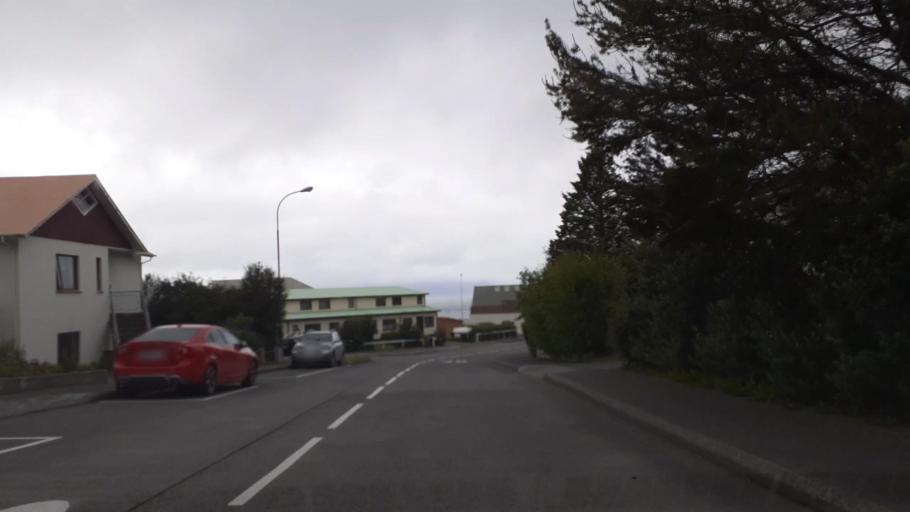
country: IS
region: Northeast
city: Husavik
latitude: 66.0406
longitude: -17.3386
